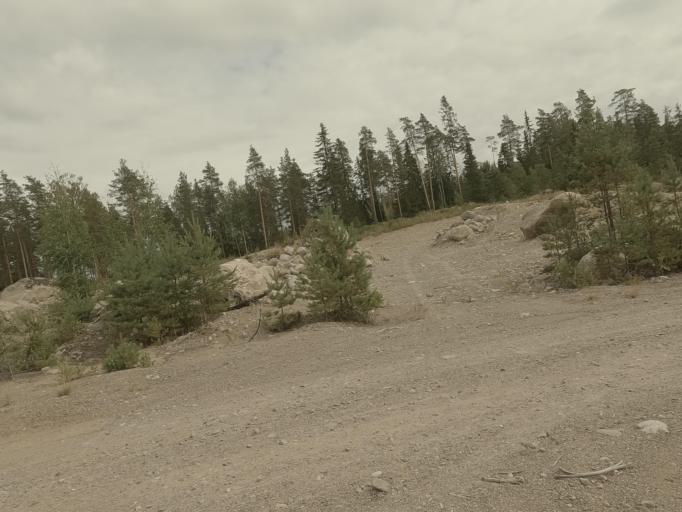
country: RU
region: Leningrad
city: Kamennogorsk
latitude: 61.0209
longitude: 29.1900
